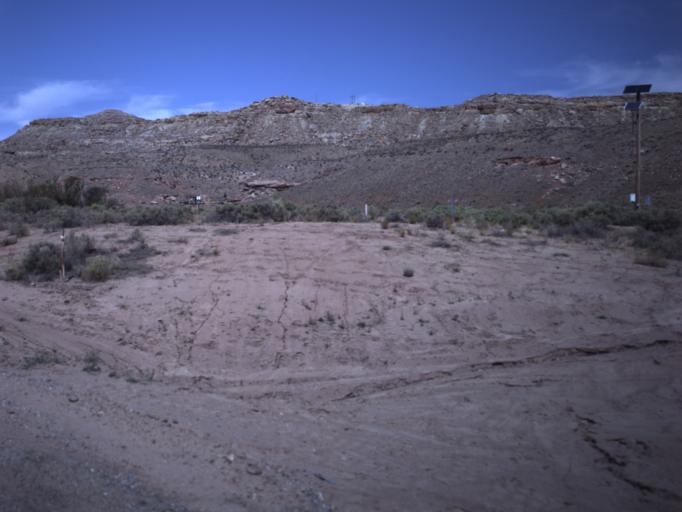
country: US
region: Utah
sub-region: San Juan County
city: Blanding
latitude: 37.2344
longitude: -109.2215
